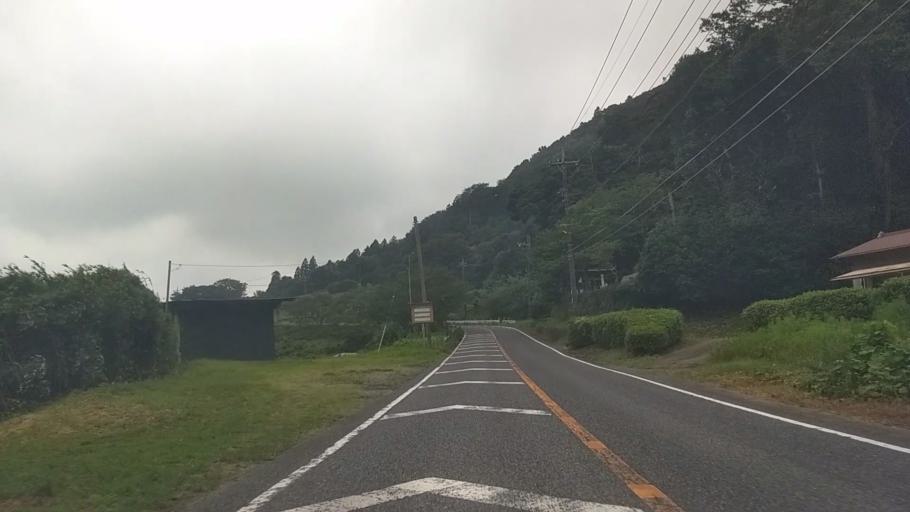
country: JP
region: Chiba
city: Tateyama
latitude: 35.1439
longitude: 139.9232
